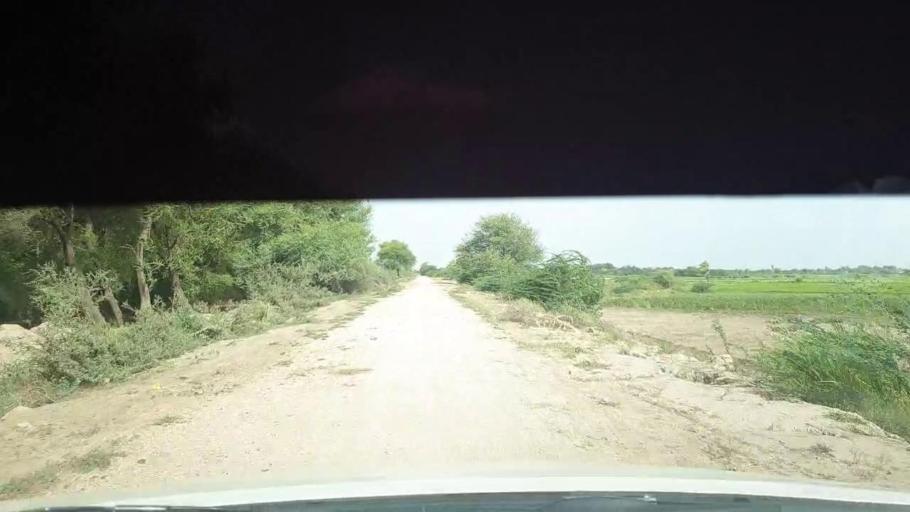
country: PK
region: Sindh
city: Kadhan
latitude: 24.5183
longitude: 69.0060
